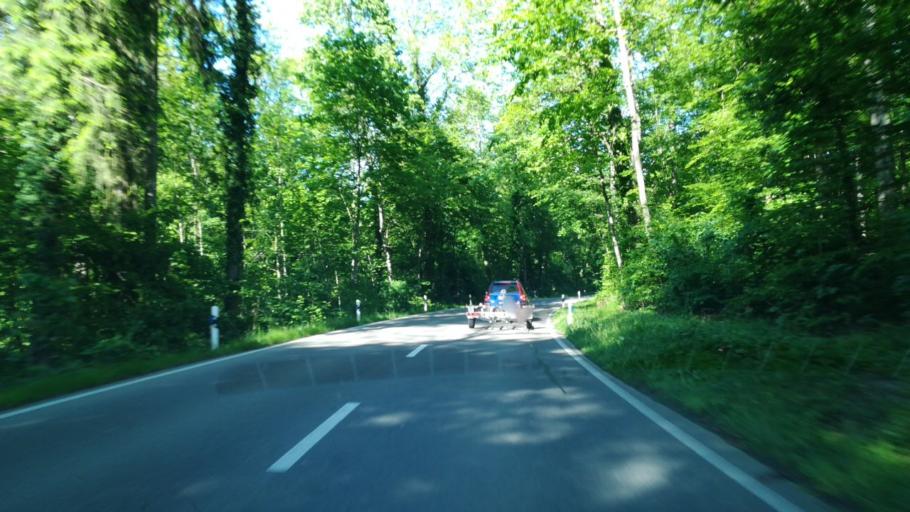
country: CH
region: Schaffhausen
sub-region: Bezirk Stein
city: Ramsen
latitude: 47.6576
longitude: 8.7948
